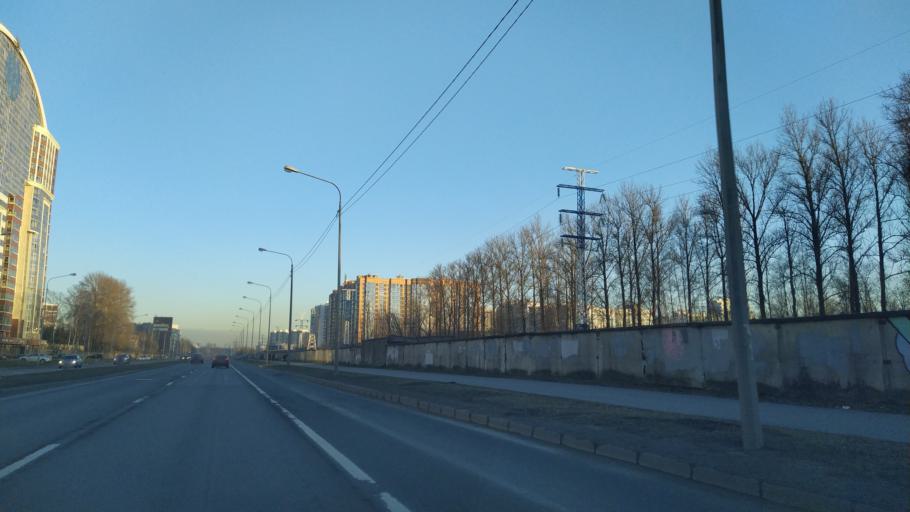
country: RU
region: St.-Petersburg
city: Kushelevka
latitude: 59.9844
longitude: 30.3672
